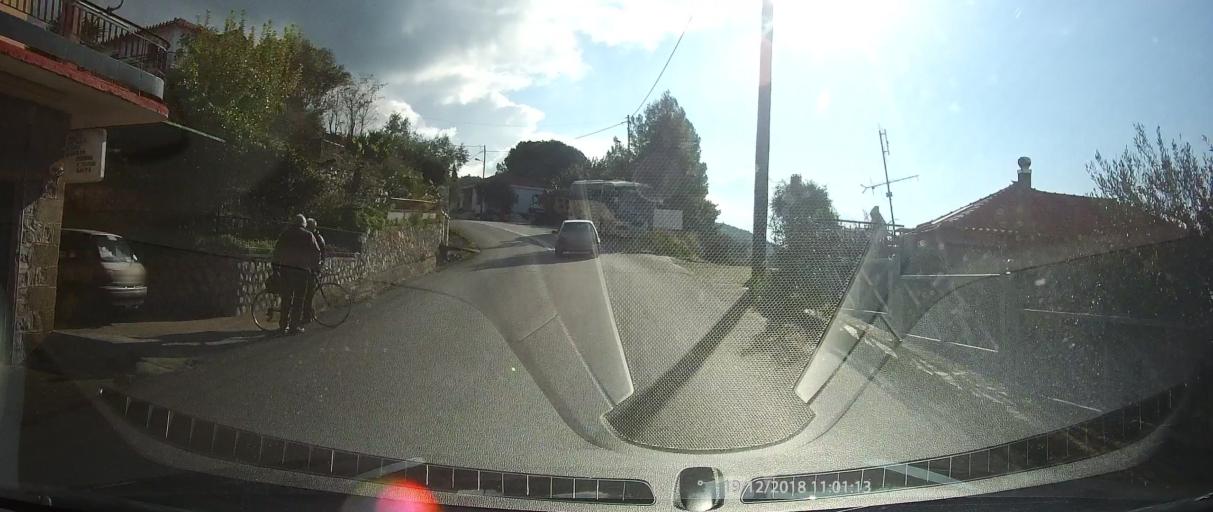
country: GR
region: Peloponnese
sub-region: Nomos Messinias
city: Kardamyli
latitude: 36.8858
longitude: 22.2337
